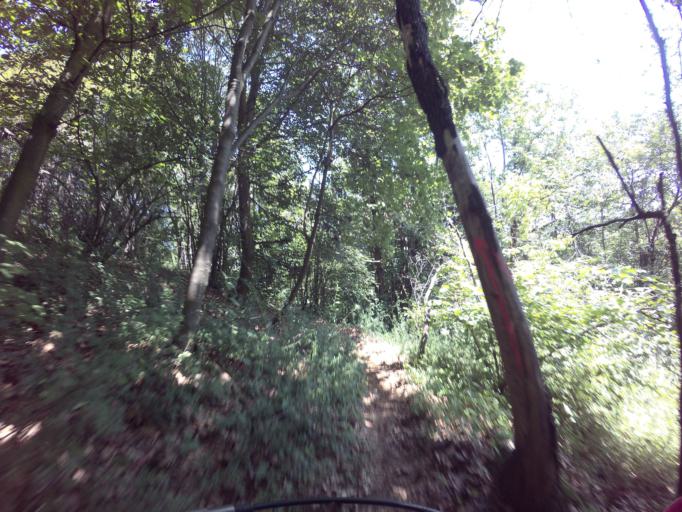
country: IT
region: Piedmont
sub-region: Provincia di Cuneo
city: Roccaforte Mondovi
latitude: 44.3323
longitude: 7.7122
